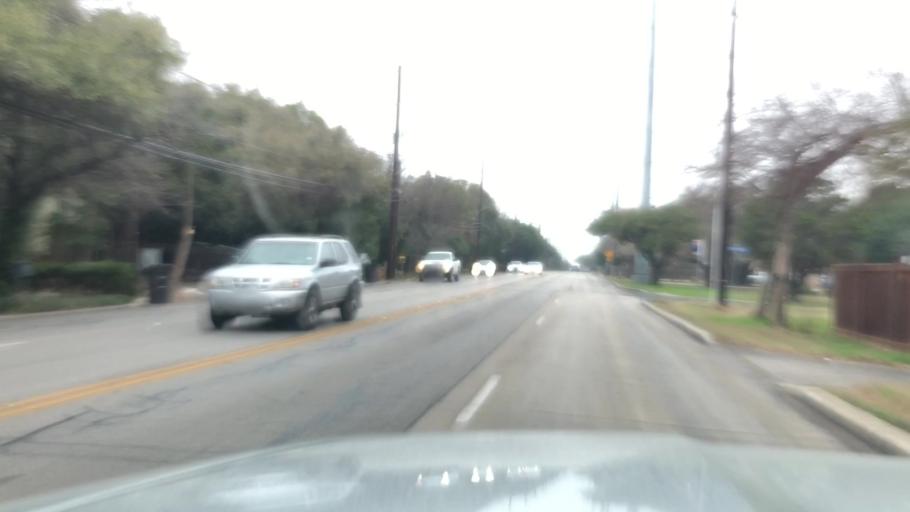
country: US
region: Texas
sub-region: Bexar County
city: Balcones Heights
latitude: 29.4959
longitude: -98.5676
